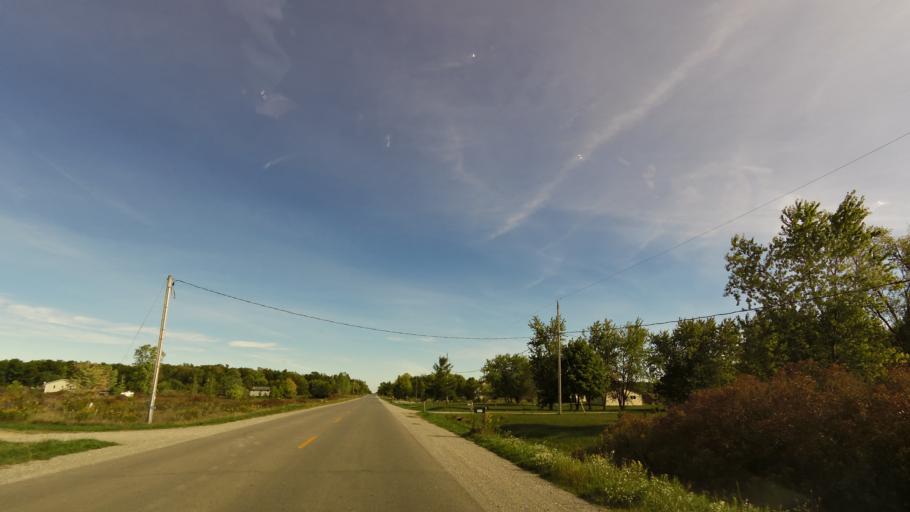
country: CA
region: Ontario
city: Ancaster
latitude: 43.0435
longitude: -80.0498
